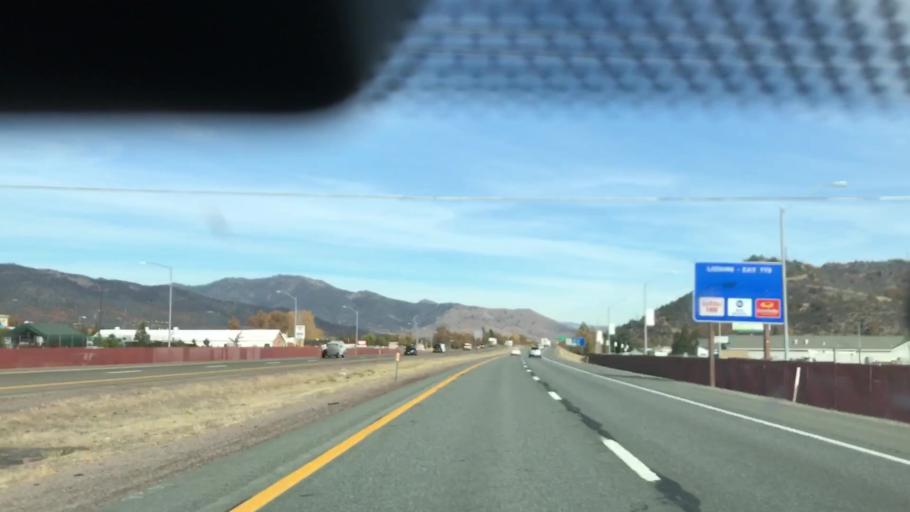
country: US
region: California
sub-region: Siskiyou County
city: Yreka
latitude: 41.7117
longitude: -122.6413
